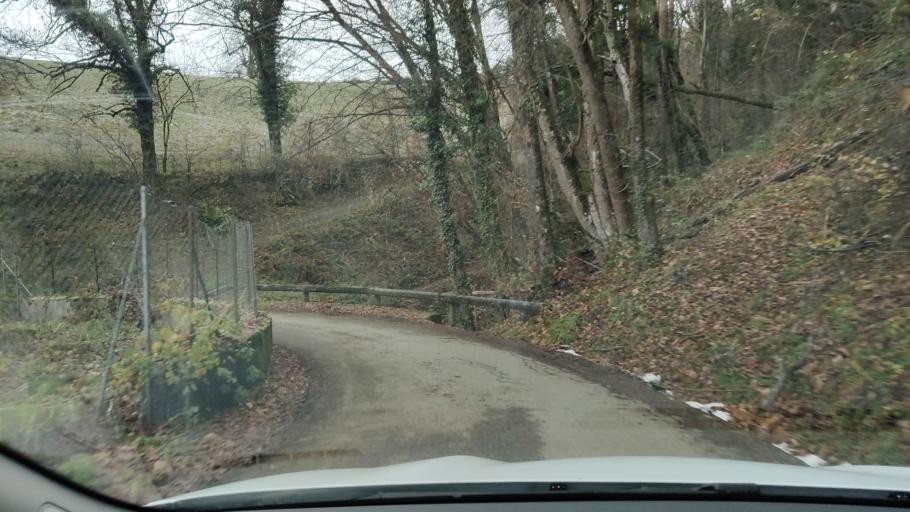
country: FR
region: Rhone-Alpes
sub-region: Departement de la Savoie
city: Montmelian
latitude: 45.4545
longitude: 6.0653
